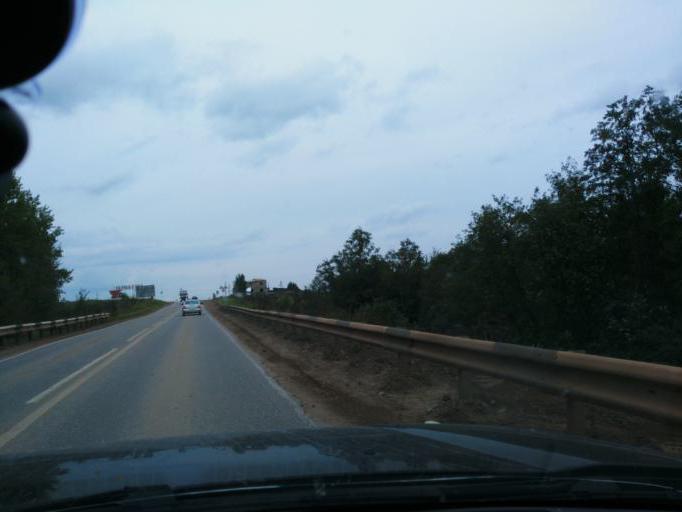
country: RU
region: Perm
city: Chernushka
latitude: 56.5427
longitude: 56.1018
